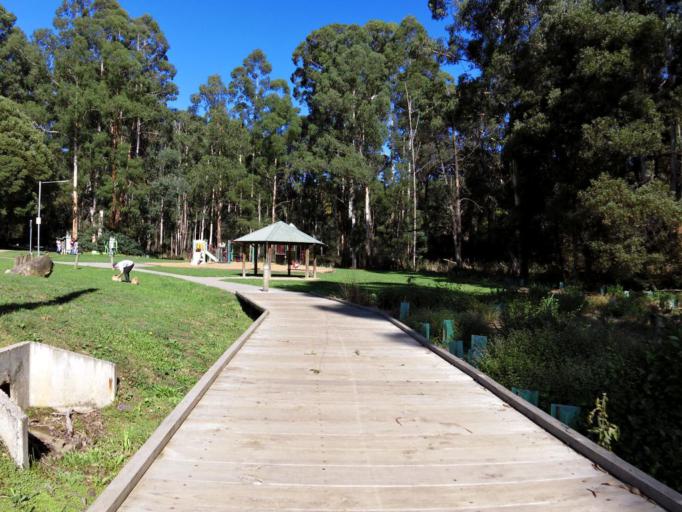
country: AU
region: Victoria
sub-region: Cardinia
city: Cockatoo
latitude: -37.9364
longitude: 145.4897
